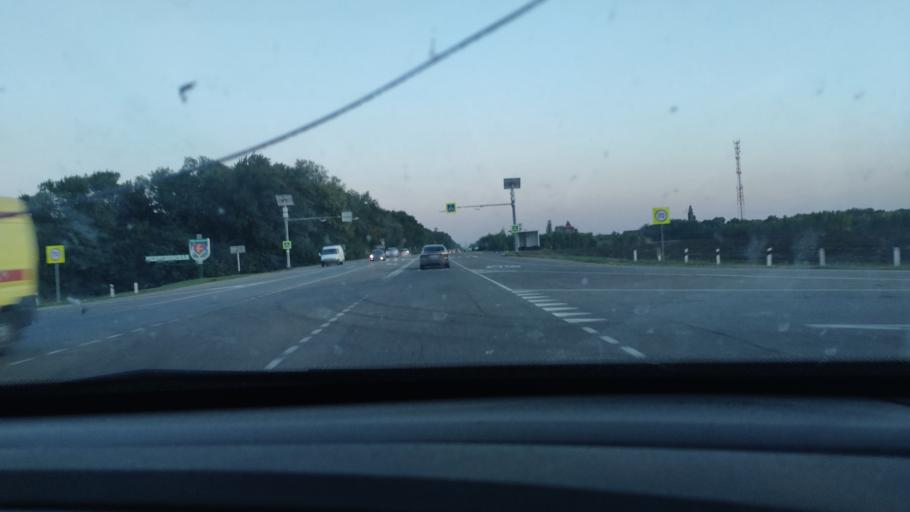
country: RU
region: Krasnodarskiy
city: Medvedovskaya
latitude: 45.4535
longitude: 38.9898
